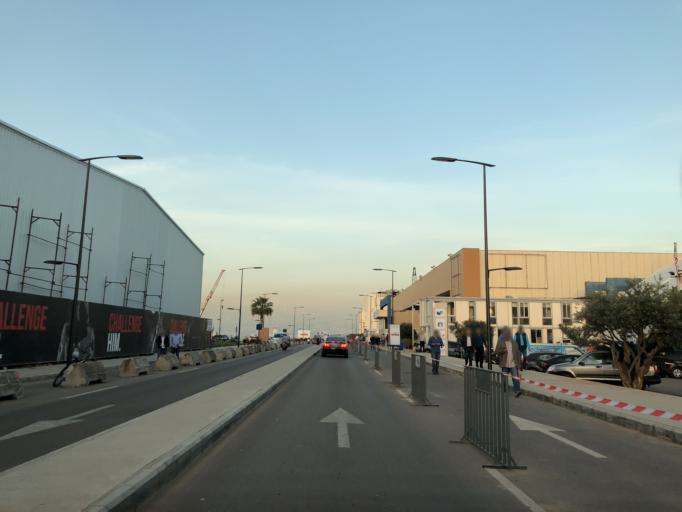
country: LB
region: Beyrouth
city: Beirut
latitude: 33.9061
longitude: 35.5082
